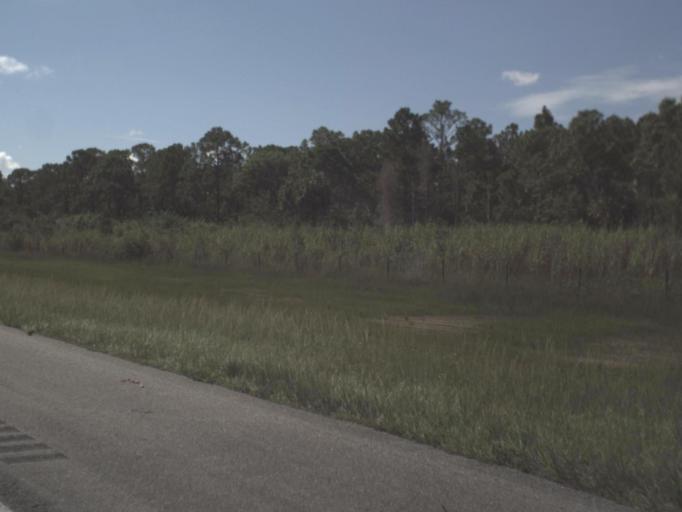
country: US
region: Florida
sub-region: Lee County
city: Burnt Store Marina
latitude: 26.8288
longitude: -81.9530
